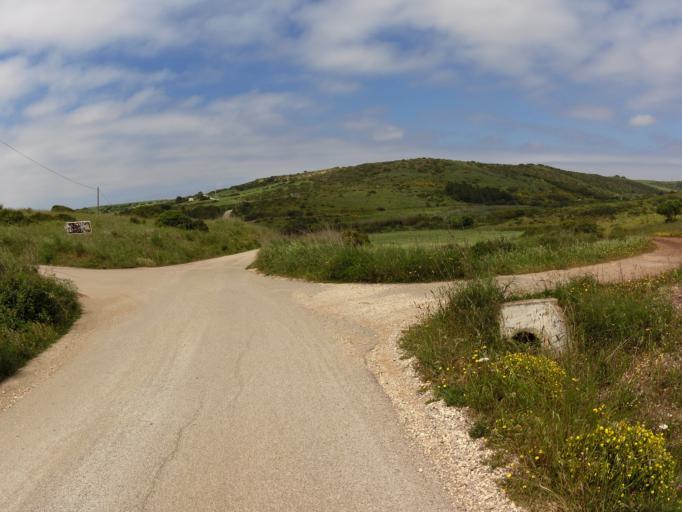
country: PT
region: Faro
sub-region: Vila do Bispo
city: Vila do Bispo
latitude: 37.0680
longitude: -8.8552
